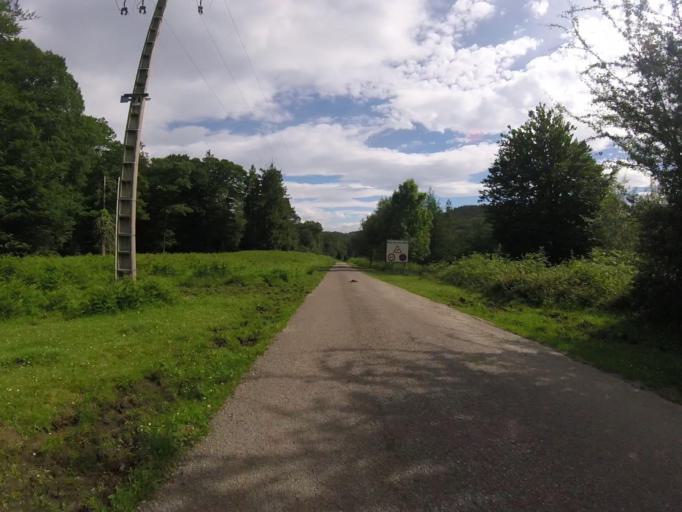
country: ES
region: Navarre
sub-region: Provincia de Navarra
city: Arantza
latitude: 43.2389
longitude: -1.8036
